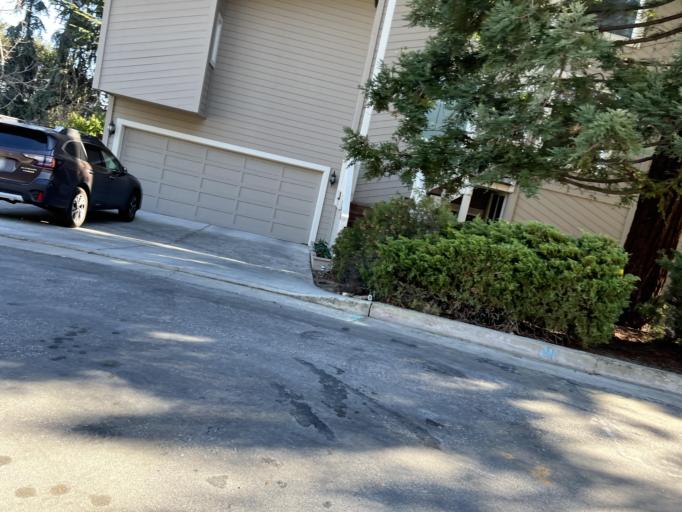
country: US
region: California
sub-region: Santa Clara County
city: Cupertino
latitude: 37.3152
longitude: -122.0740
